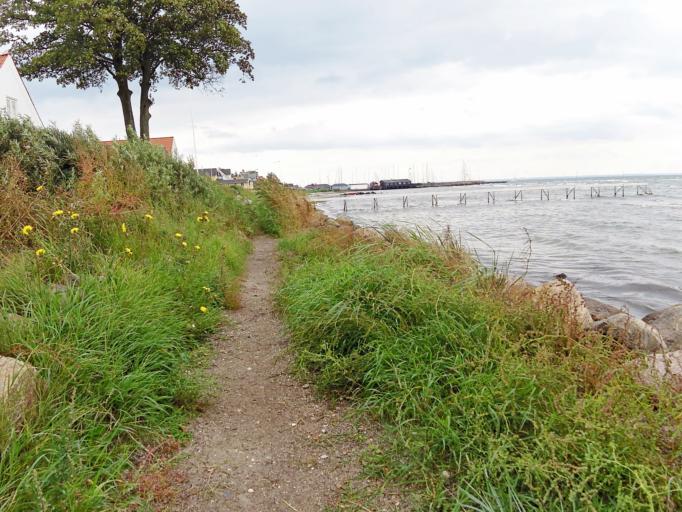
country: DK
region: Capital Region
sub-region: Fredensborg Kommune
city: Humlebaek
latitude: 55.9511
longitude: 12.5328
